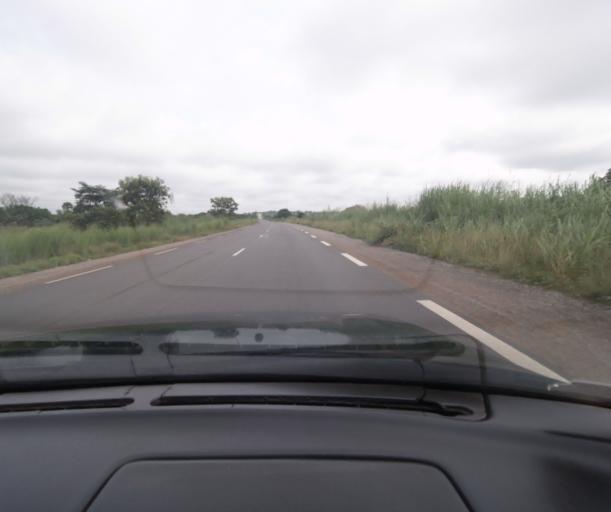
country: CM
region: Centre
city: Saa
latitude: 4.3892
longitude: 11.2548
